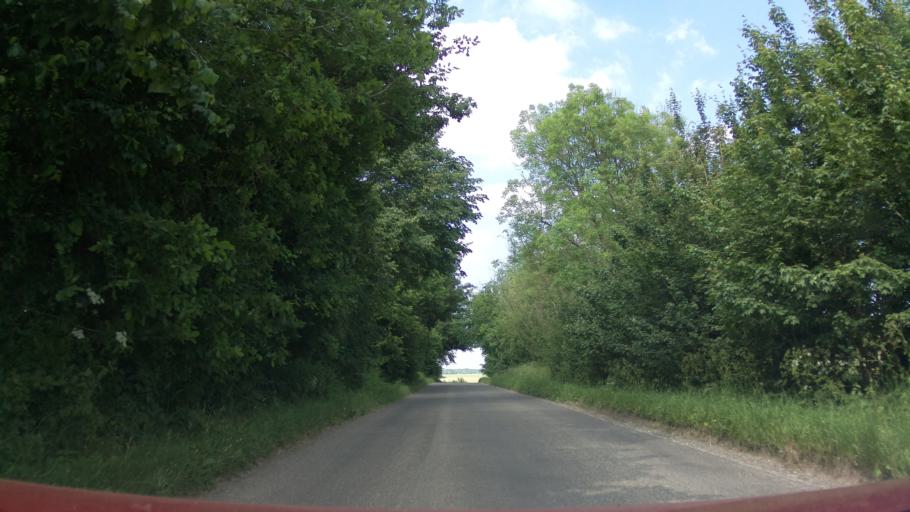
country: GB
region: England
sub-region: Wiltshire
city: Milston
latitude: 51.2586
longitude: -1.7303
